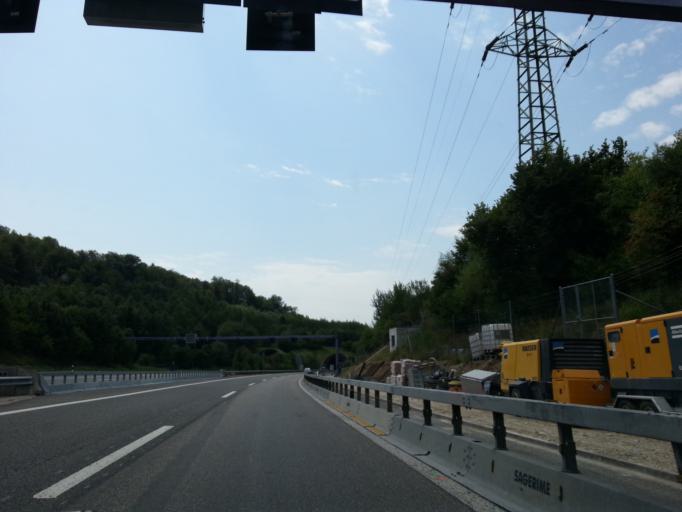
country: CH
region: Fribourg
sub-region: See District
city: Murten
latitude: 46.9197
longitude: 7.1284
